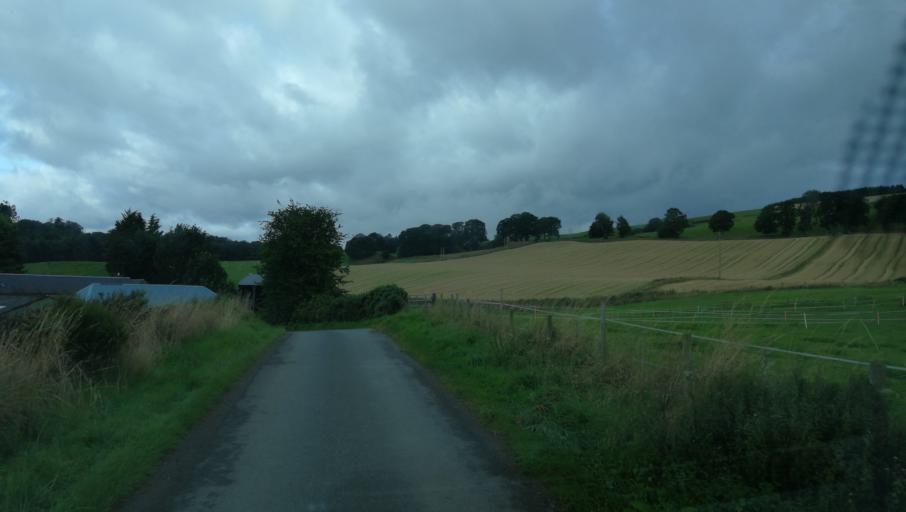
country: GB
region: Scotland
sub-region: Perth and Kinross
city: Blairgowrie
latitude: 56.6039
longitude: -3.3100
